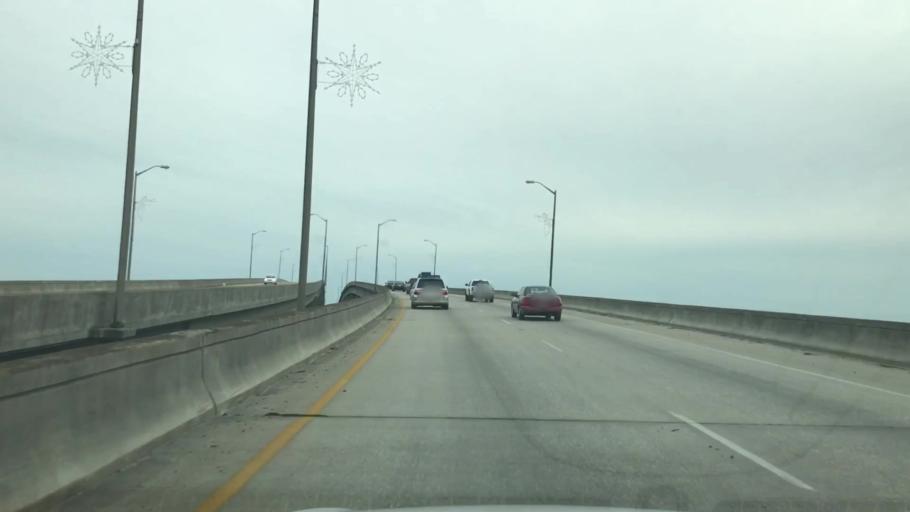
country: US
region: South Carolina
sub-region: Georgetown County
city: Georgetown
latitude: 33.3618
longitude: -79.2954
